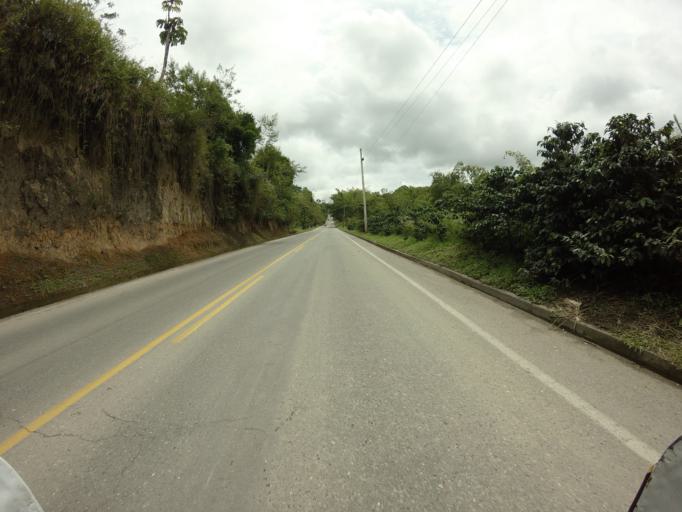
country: CO
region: Quindio
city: Quimbaya
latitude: 4.6353
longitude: -75.7735
